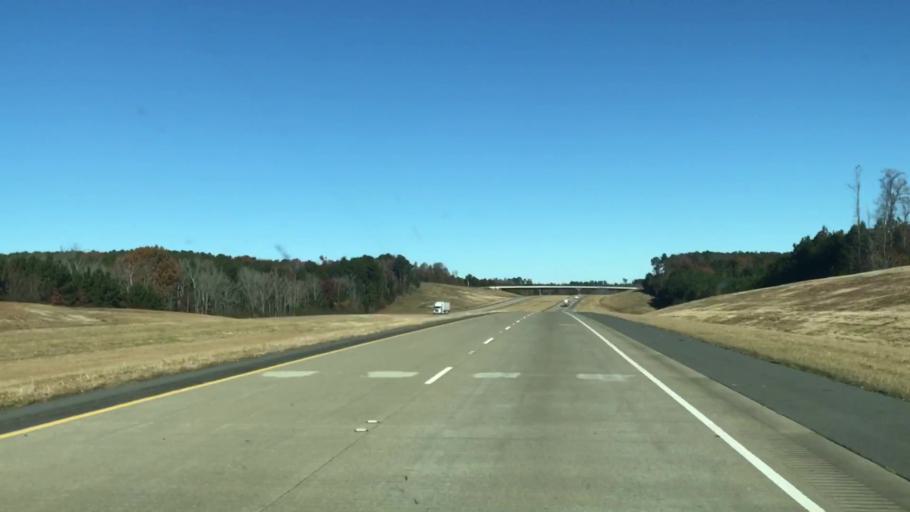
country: US
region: Louisiana
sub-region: Caddo Parish
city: Vivian
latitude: 32.9710
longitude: -93.9072
